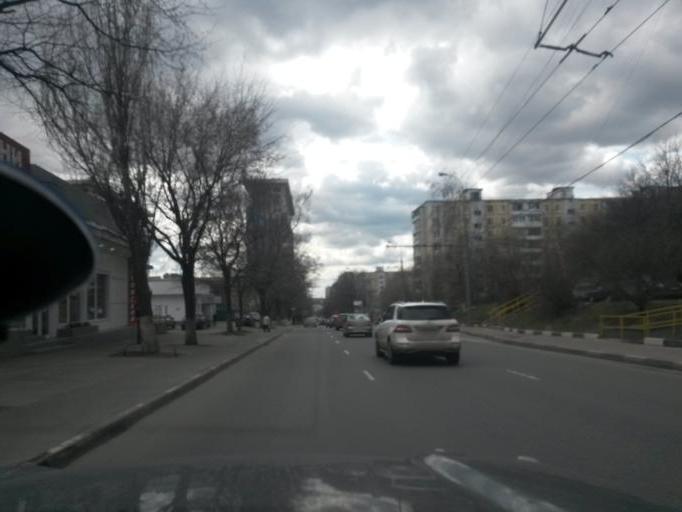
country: RU
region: Moscow
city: Yasenevo
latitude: 55.6122
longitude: 37.5365
